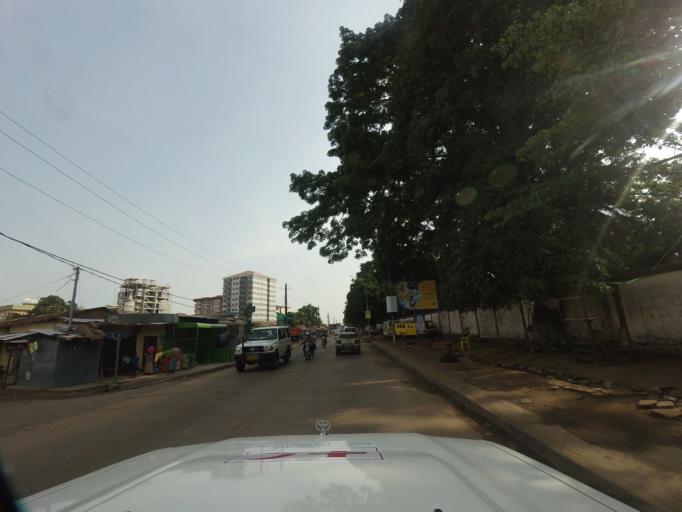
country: GN
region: Conakry
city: Camayenne
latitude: 9.5291
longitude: -13.6877
